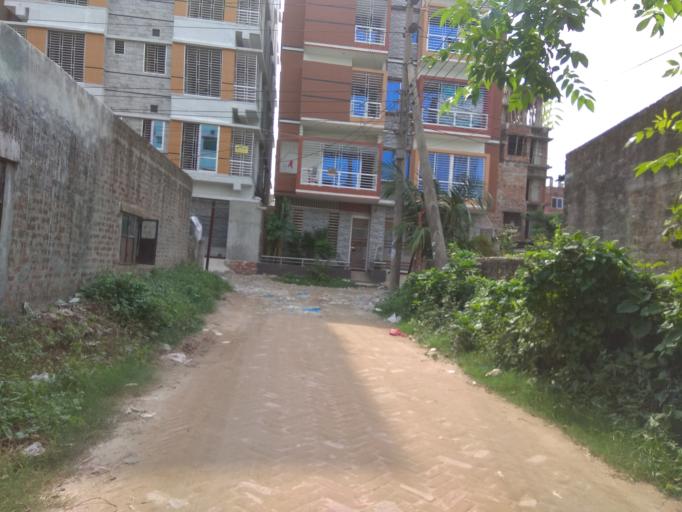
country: BD
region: Dhaka
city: Tungi
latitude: 23.8307
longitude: 90.3503
